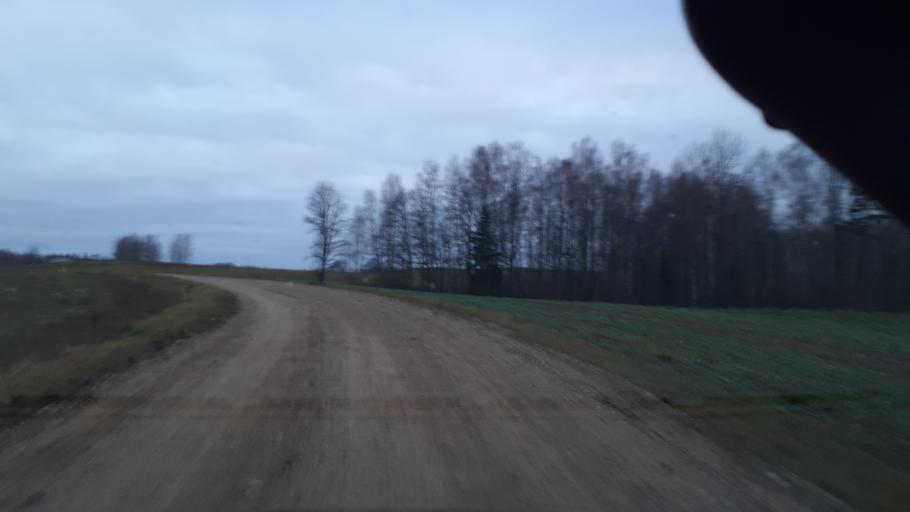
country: LV
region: Alsunga
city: Alsunga
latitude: 56.8903
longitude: 21.6932
